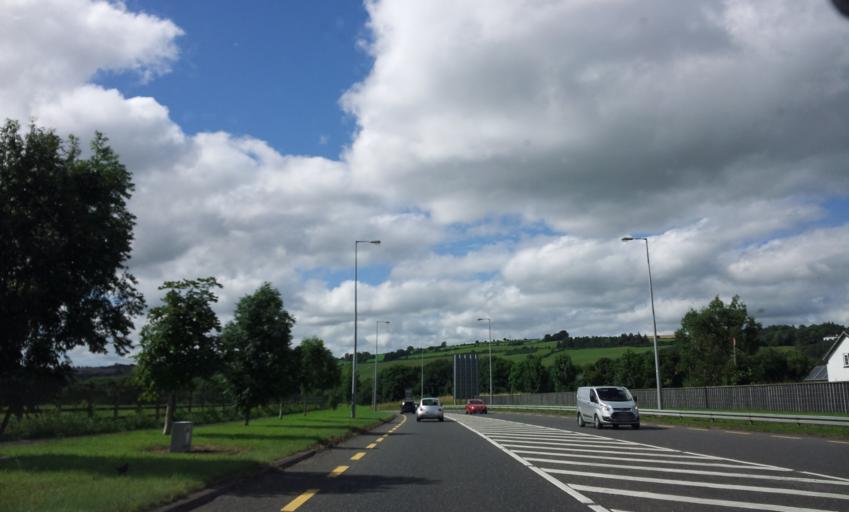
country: IE
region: Munster
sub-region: County Cork
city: Killumney
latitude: 51.8788
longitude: -8.6489
